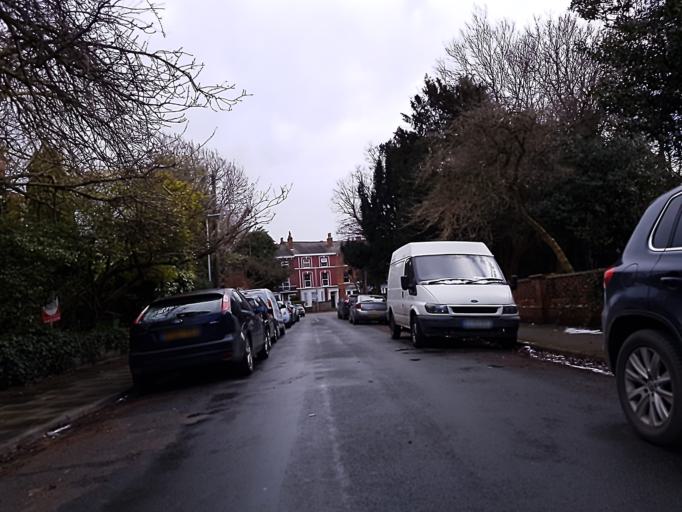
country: GB
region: England
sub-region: North East Lincolnshire
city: Grimbsy
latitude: 53.5620
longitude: -0.0931
